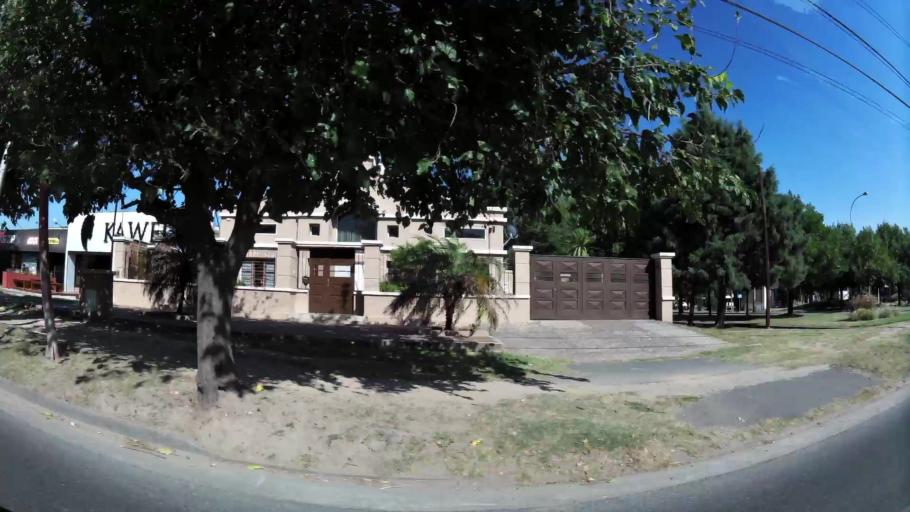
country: AR
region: Cordoba
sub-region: Departamento de Capital
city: Cordoba
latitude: -31.4628
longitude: -64.1869
